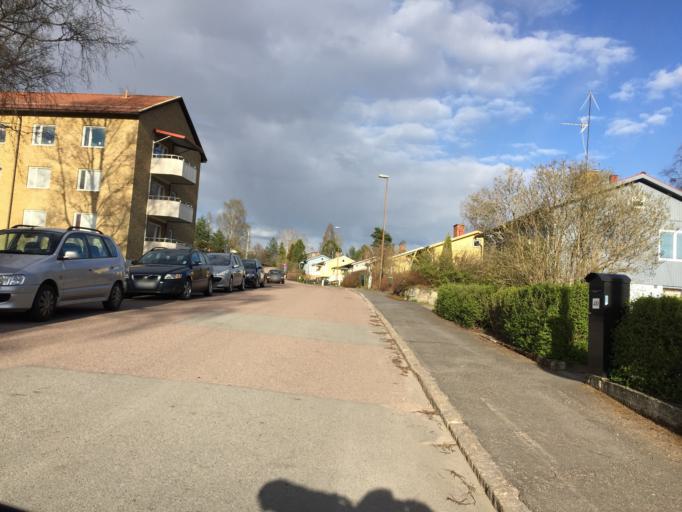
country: SE
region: Dalarna
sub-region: Ludvika Kommun
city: Ludvika
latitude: 60.1300
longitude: 15.1669
